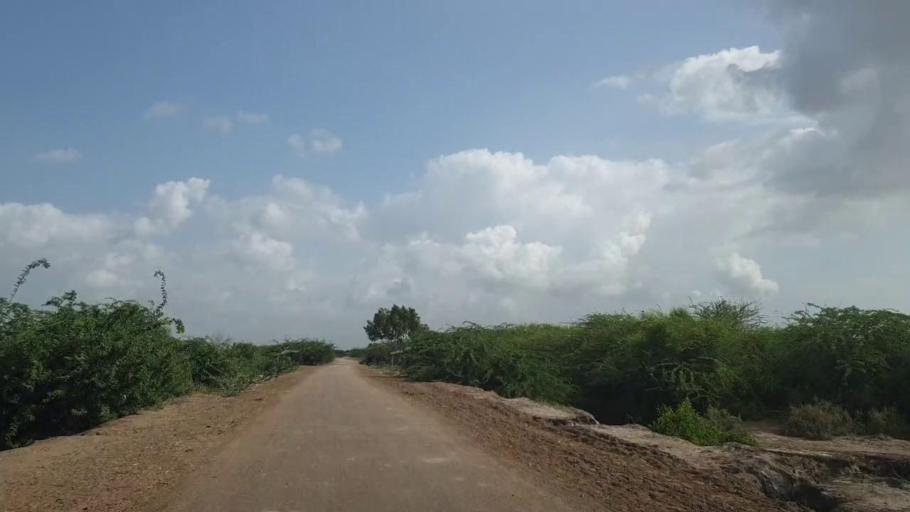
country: PK
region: Sindh
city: Kadhan
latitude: 24.5541
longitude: 69.0637
